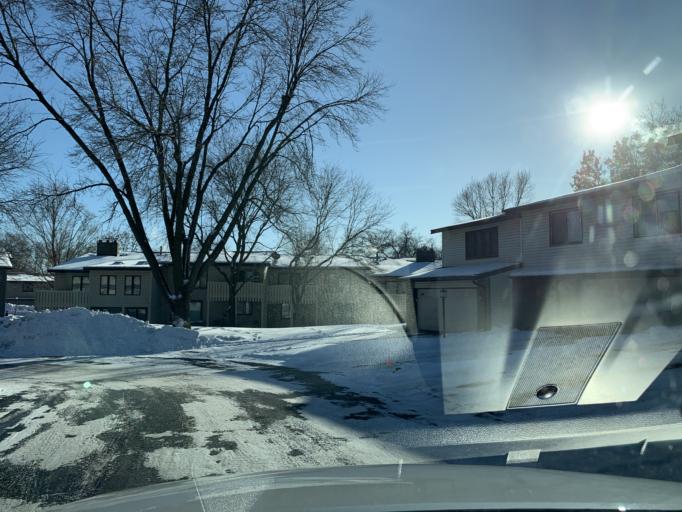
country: US
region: Minnesota
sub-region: Scott County
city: Savage
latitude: 44.8286
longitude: -93.3577
